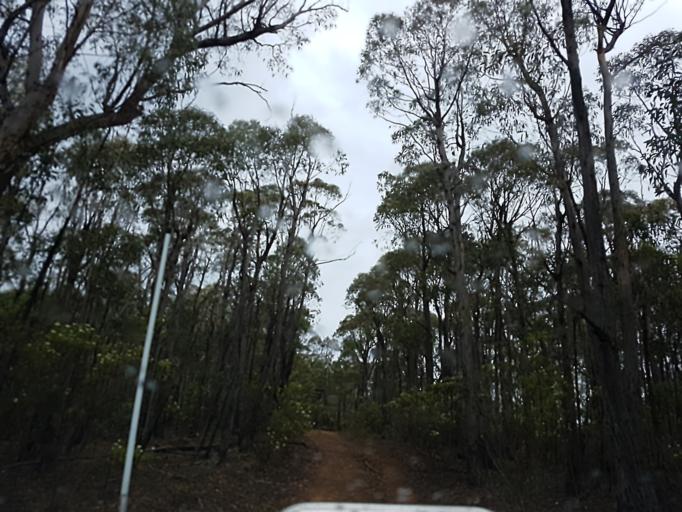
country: AU
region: New South Wales
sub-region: Snowy River
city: Jindabyne
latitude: -36.8738
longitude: 148.3320
